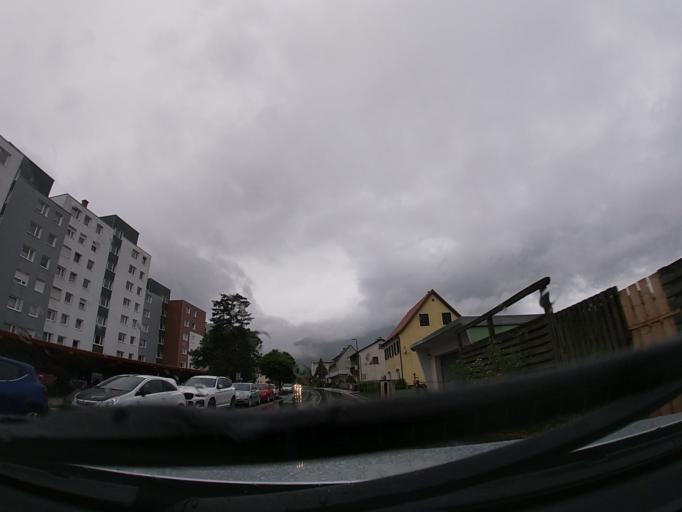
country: AT
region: Styria
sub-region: Politischer Bezirk Leoben
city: Trofaiach
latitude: 47.4245
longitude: 14.9949
